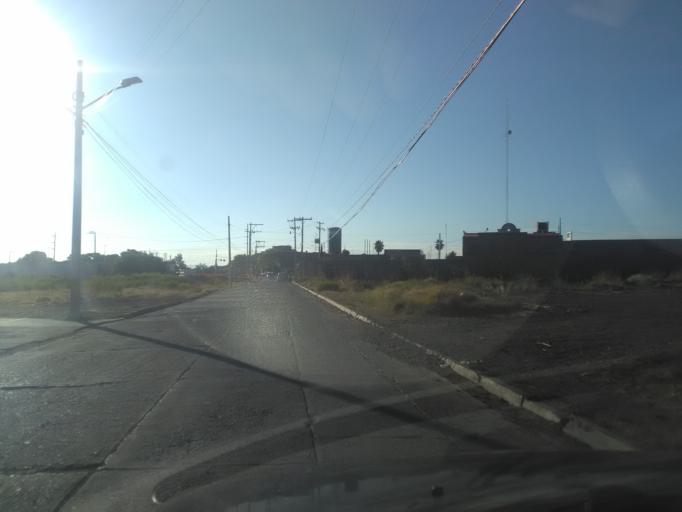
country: MX
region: Durango
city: Victoria de Durango
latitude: 24.0005
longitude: -104.7017
